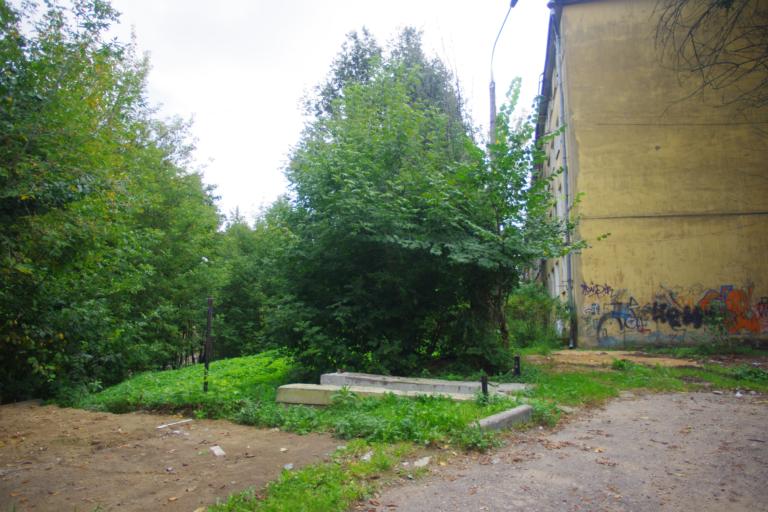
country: RU
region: Moskovskaya
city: Krasnogorsk
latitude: 55.8345
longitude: 37.3264
